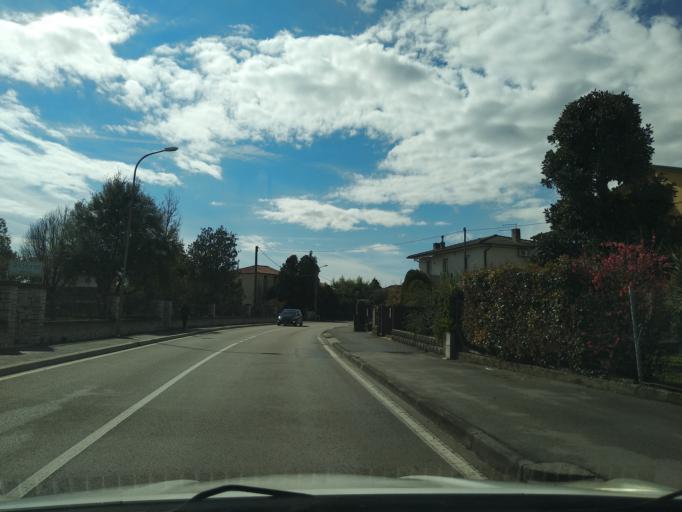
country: IT
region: Veneto
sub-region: Provincia di Vicenza
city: Vigardolo
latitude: 45.6031
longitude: 11.5901
